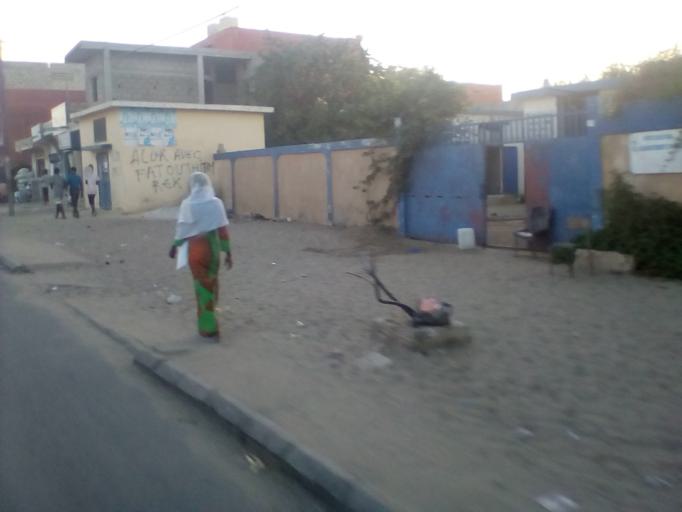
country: SN
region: Saint-Louis
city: Saint-Louis
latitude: 16.0178
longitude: -16.4906
